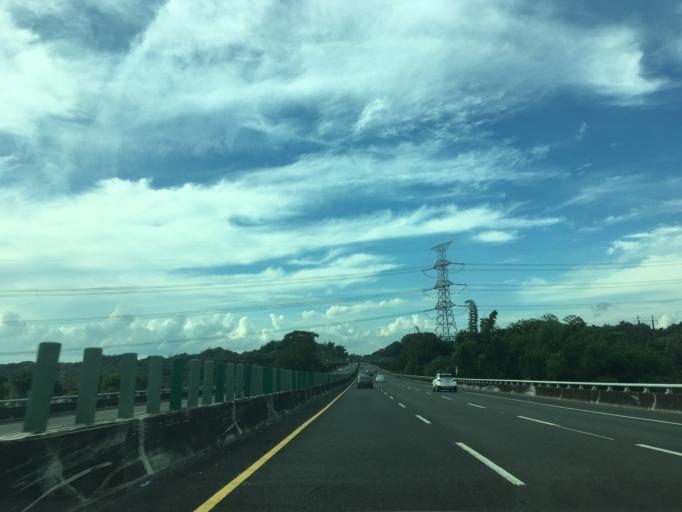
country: TW
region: Taiwan
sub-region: Chiayi
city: Jiayi Shi
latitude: 23.5550
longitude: 120.5051
